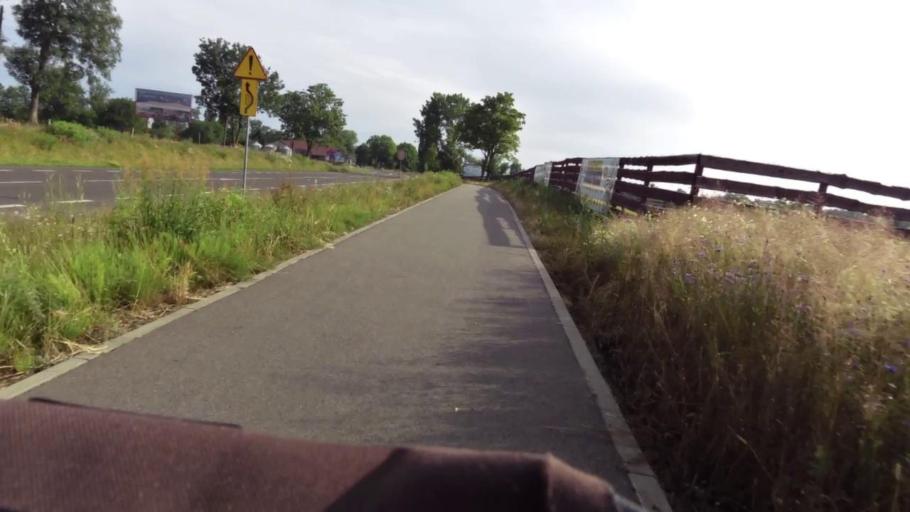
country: PL
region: West Pomeranian Voivodeship
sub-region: Powiat kamienski
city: Kamien Pomorski
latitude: 53.9947
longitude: 14.8170
